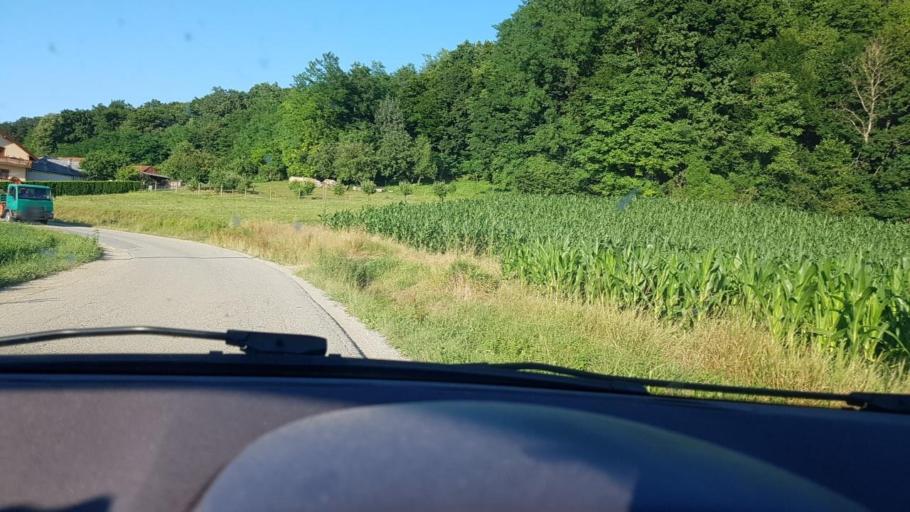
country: HR
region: Krapinsko-Zagorska
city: Zabok
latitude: 46.0803
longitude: 15.9305
